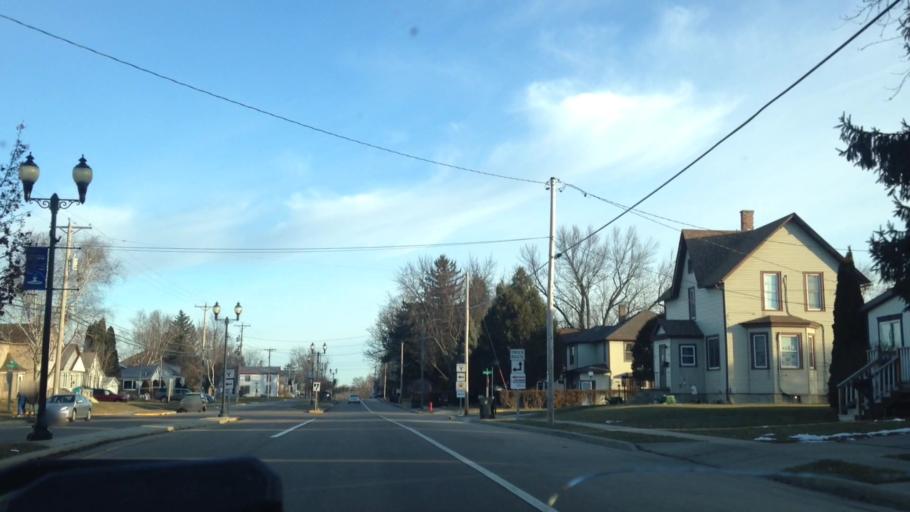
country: US
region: Wisconsin
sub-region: Dodge County
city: Mayville
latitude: 43.5015
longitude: -88.5440
